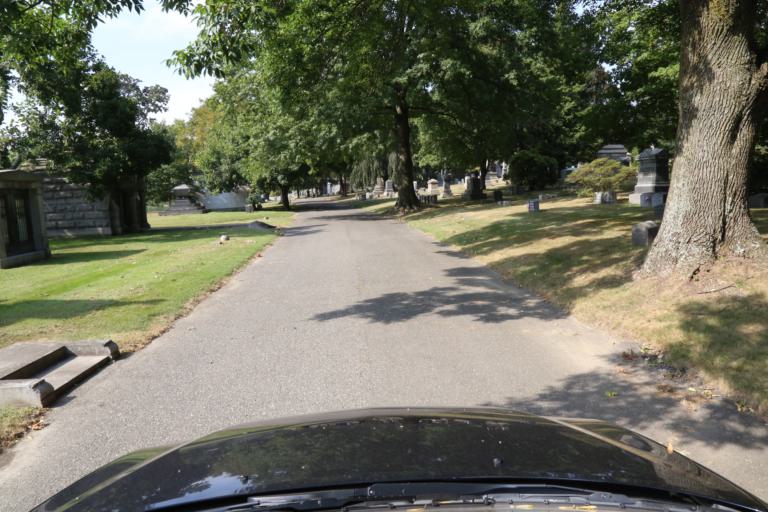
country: US
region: New York
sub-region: Bronx
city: Eastchester
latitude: 40.8925
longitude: -73.8696
